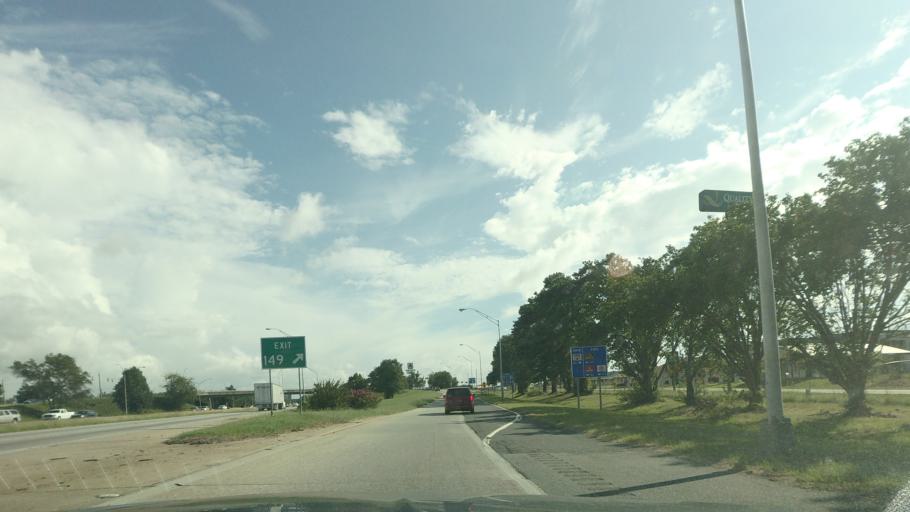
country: US
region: Georgia
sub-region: Peach County
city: Byron
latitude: 32.6615
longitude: -83.7446
